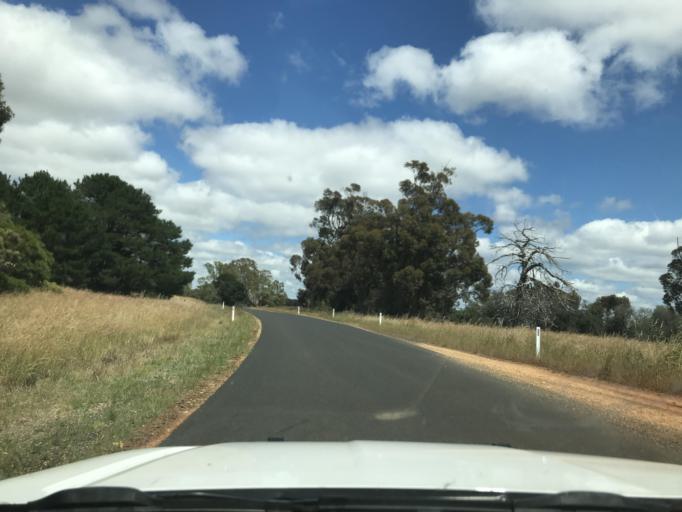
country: AU
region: South Australia
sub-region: Naracoorte and Lucindale
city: Naracoorte
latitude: -36.6673
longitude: 141.2832
